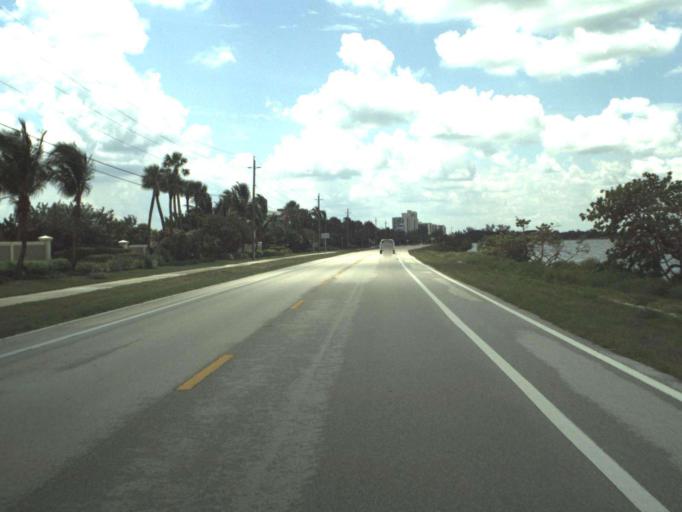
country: US
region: Florida
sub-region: Saint Lucie County
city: Hutchinson Island South
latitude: 27.3191
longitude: -80.2267
